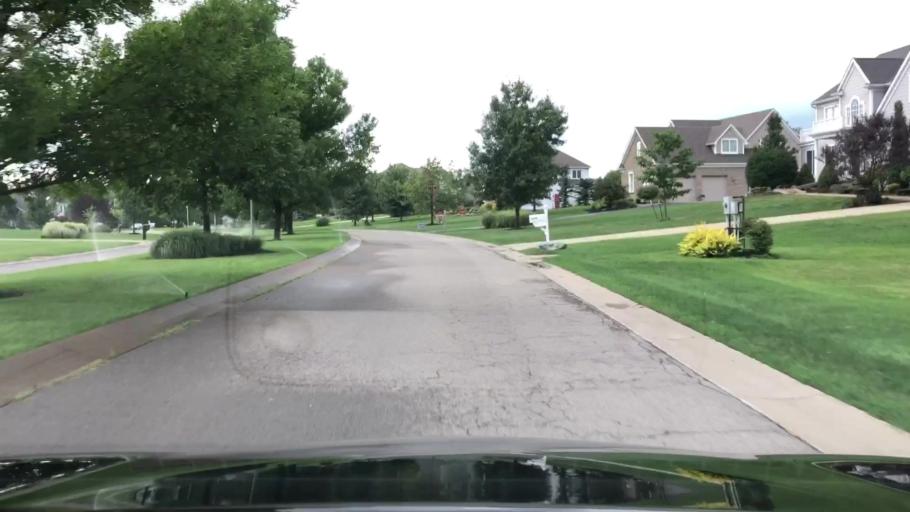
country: US
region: New York
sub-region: Erie County
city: Orchard Park
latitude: 42.7524
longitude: -78.7181
